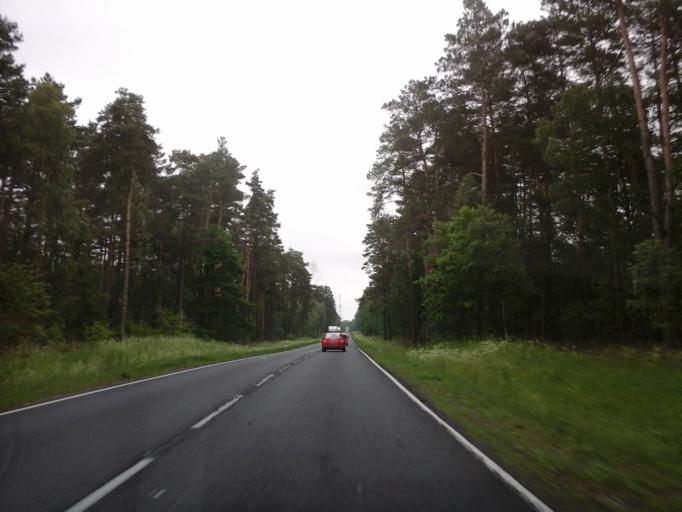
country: PL
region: West Pomeranian Voivodeship
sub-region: Powiat walecki
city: Miroslawiec
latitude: 53.3218
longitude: 16.0083
